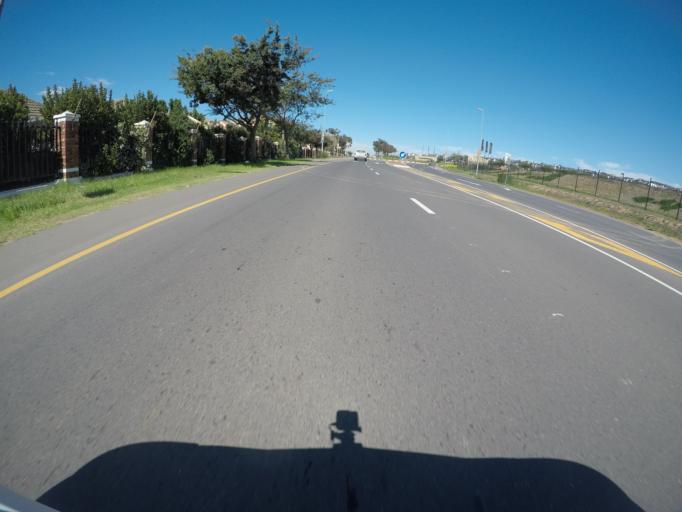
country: ZA
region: Western Cape
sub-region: City of Cape Town
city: Kraaifontein
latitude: -33.8175
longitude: 18.6344
